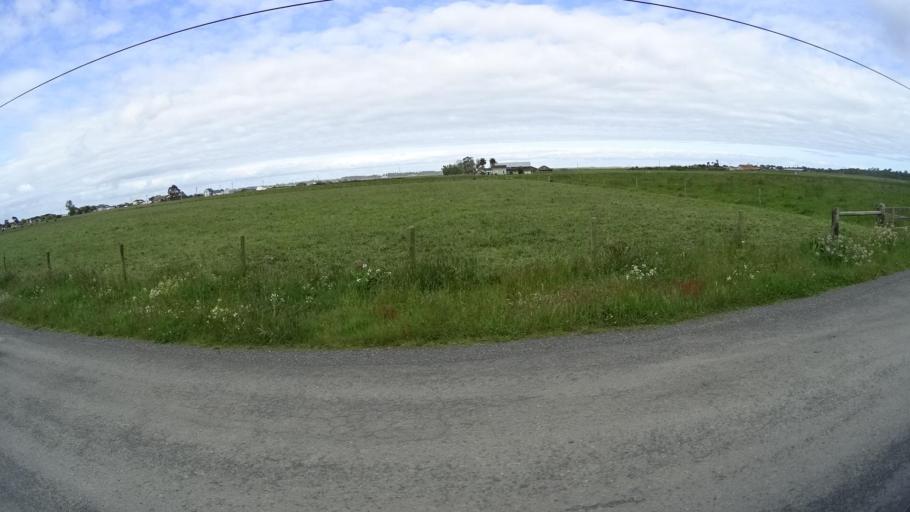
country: US
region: California
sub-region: Humboldt County
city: Arcata
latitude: 40.9047
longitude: -124.0914
